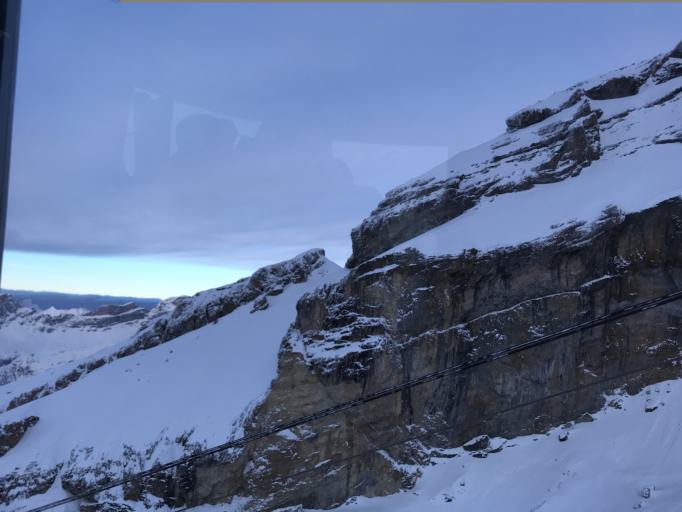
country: CH
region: Obwalden
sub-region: Obwalden
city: Engelberg
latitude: 46.7766
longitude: 8.4201
